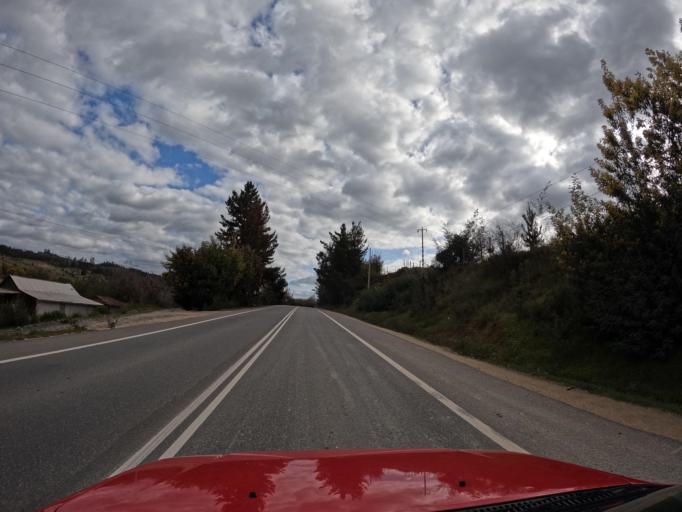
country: CL
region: Maule
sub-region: Provincia de Linares
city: San Javier
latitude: -35.5588
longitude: -72.0900
